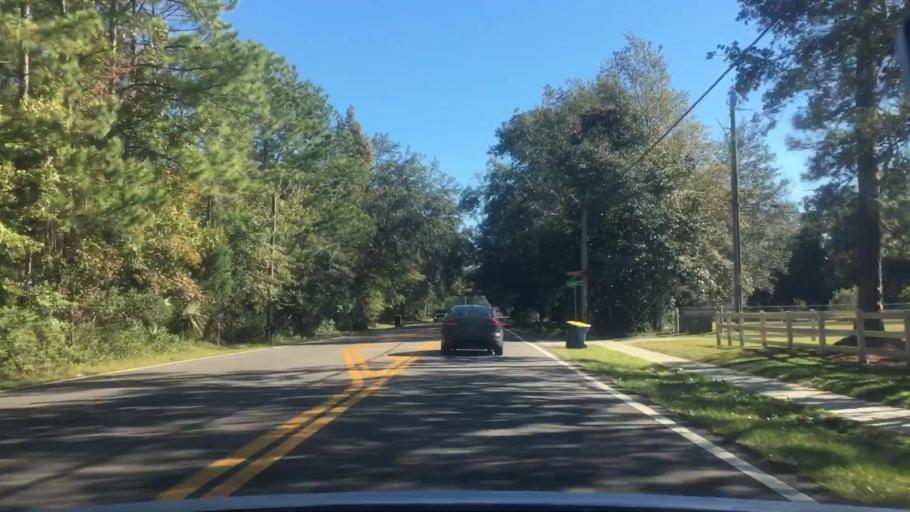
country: US
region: Florida
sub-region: Nassau County
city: Yulee
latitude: 30.4841
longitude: -81.5957
